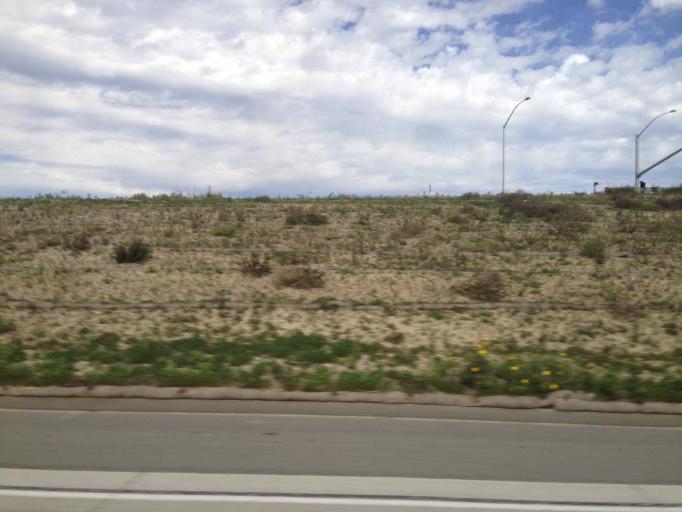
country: MX
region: Baja California
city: Tijuana
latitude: 32.5666
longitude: -117.0150
